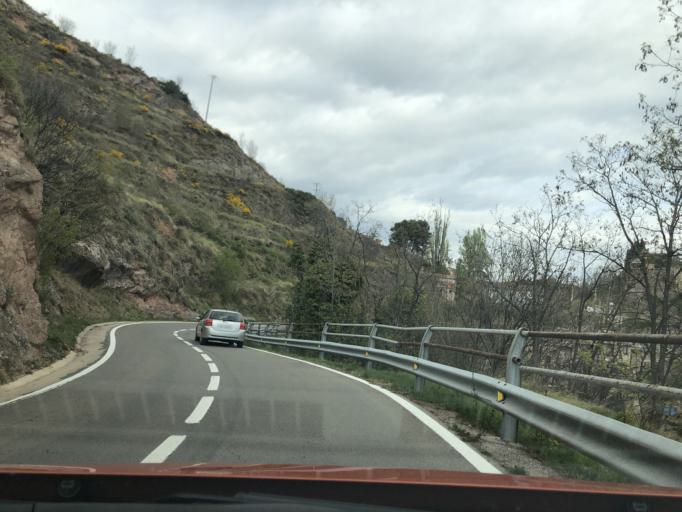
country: ES
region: Catalonia
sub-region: Provincia de Barcelona
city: Berga
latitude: 42.1053
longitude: 1.8433
